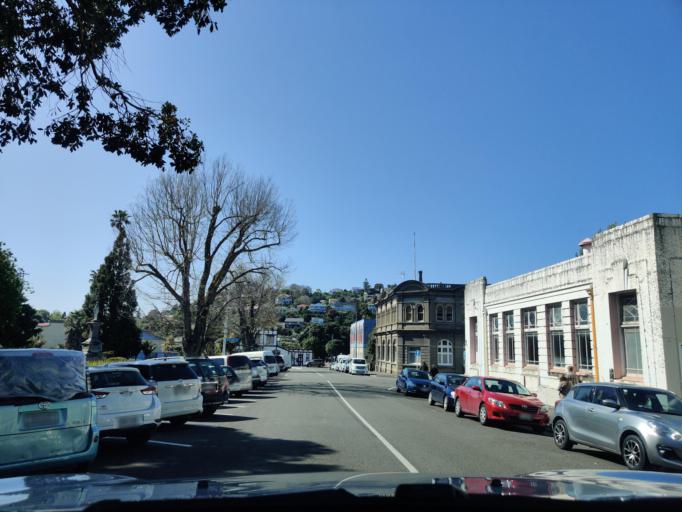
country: NZ
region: Manawatu-Wanganui
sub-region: Wanganui District
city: Wanganui
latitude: -39.9321
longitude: 175.0563
